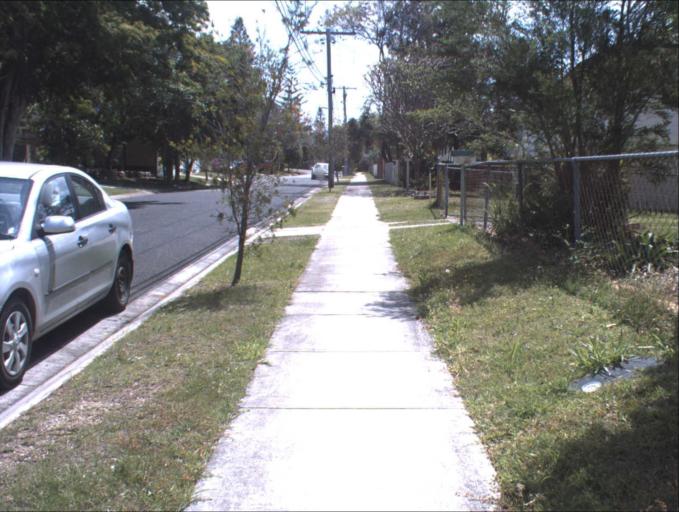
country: AU
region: Queensland
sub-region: Logan
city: Woodridge
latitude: -27.6194
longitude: 153.0994
